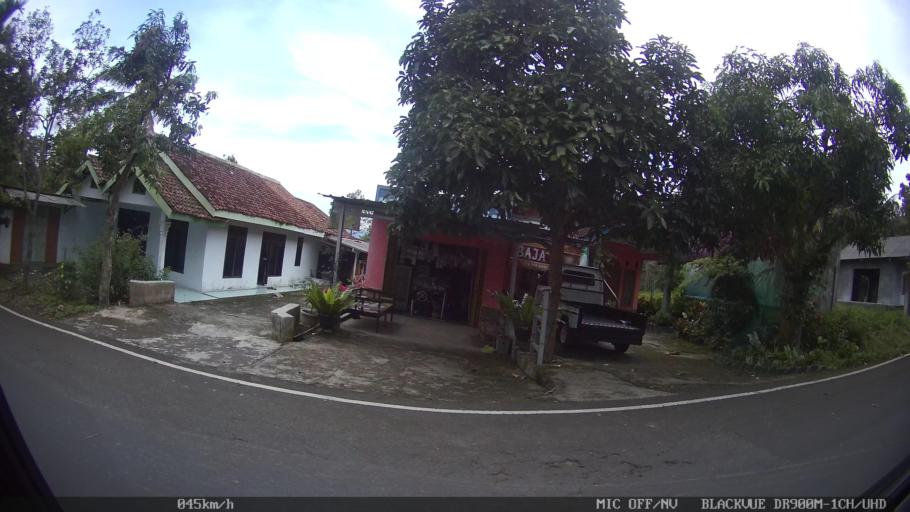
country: ID
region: Lampung
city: Bandarlampung
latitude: -5.4215
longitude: 105.1907
